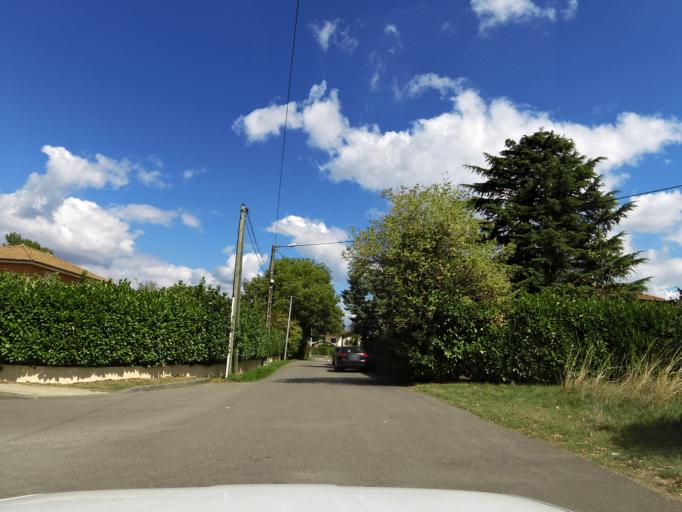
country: FR
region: Rhone-Alpes
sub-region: Departement de l'Ain
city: Meximieux
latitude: 45.9085
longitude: 5.2089
